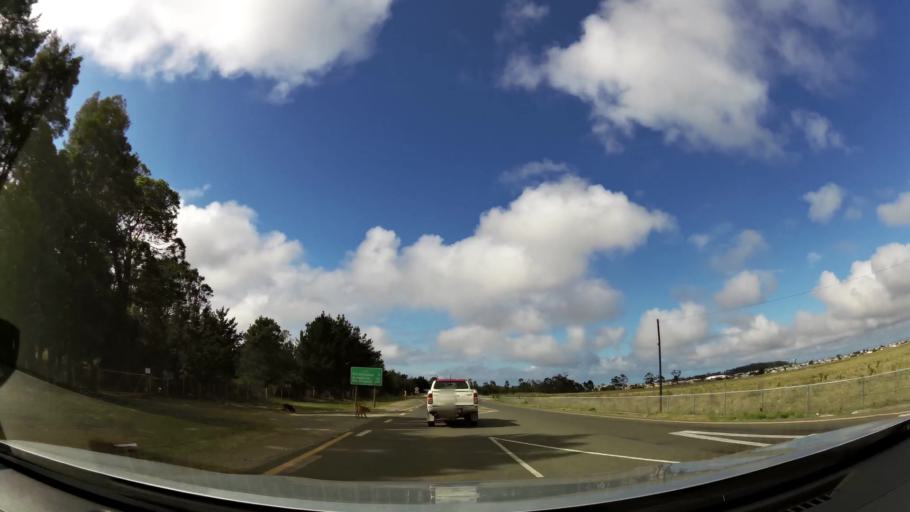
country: ZA
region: Western Cape
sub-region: Eden District Municipality
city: Plettenberg Bay
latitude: -34.0443
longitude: 23.3095
